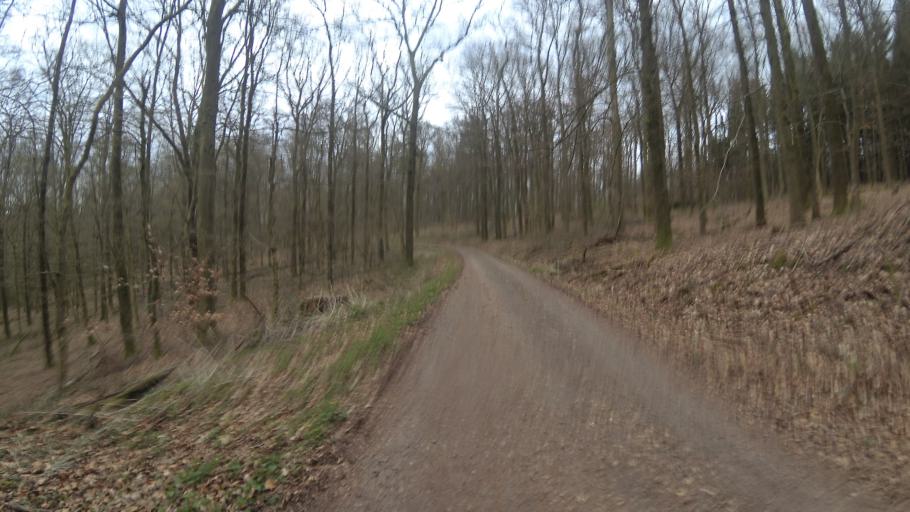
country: DE
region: Saarland
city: Hangard
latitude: 49.4320
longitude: 7.2133
